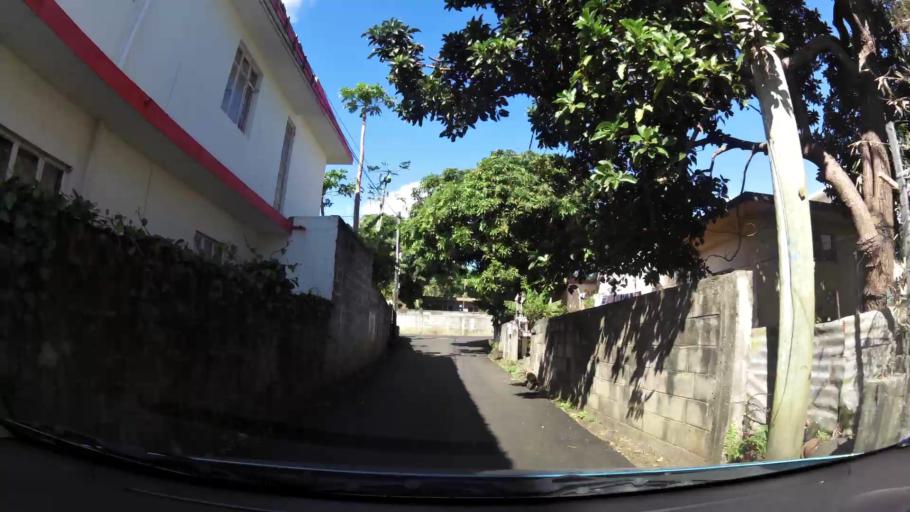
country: MU
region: Plaines Wilhems
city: Vacoas
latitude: -20.2897
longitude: 57.4761
